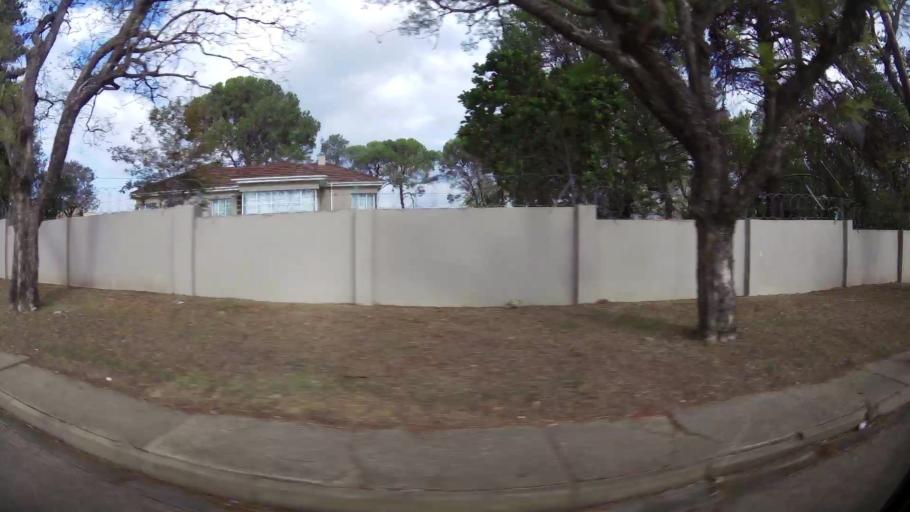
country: ZA
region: Eastern Cape
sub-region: Nelson Mandela Bay Metropolitan Municipality
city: Uitenhage
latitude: -33.7470
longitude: 25.4014
